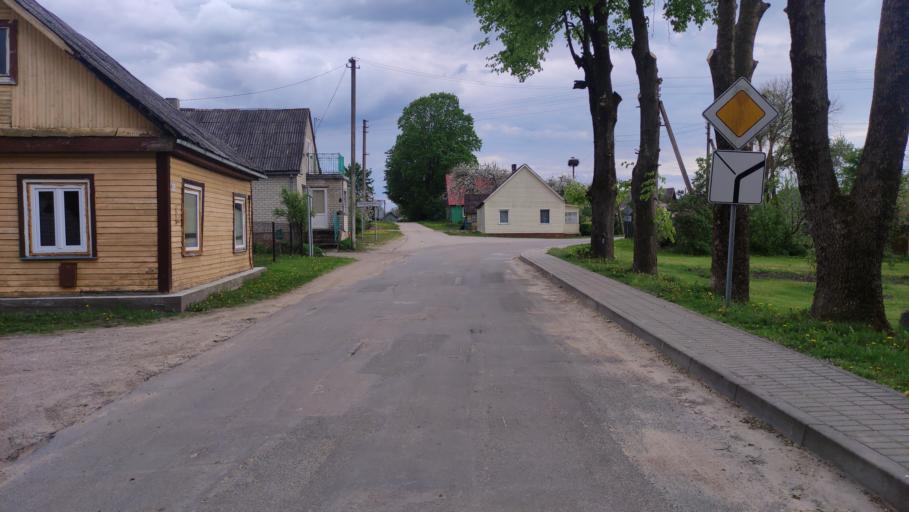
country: LT
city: Jieznas
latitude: 54.5033
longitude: 24.2544
